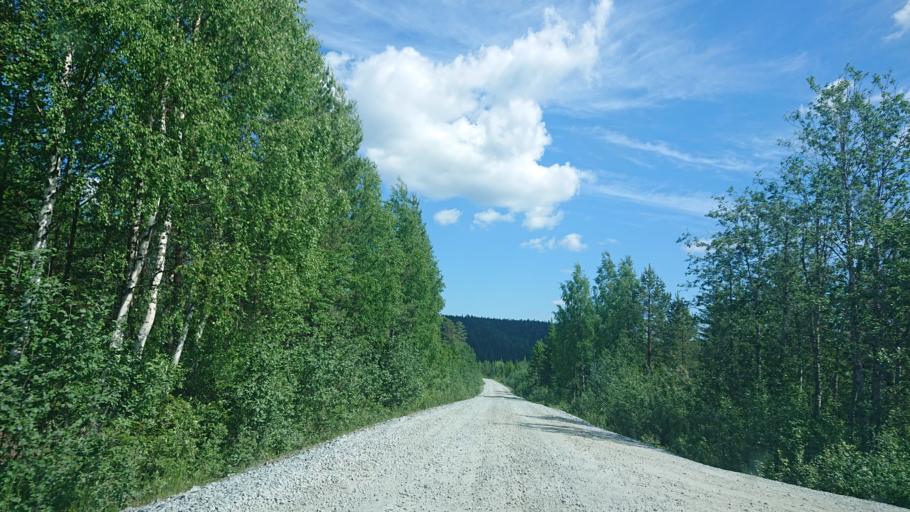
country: SE
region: Vaesternorrland
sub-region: Solleftea Kommun
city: Solleftea
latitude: 62.9334
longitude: 17.1164
